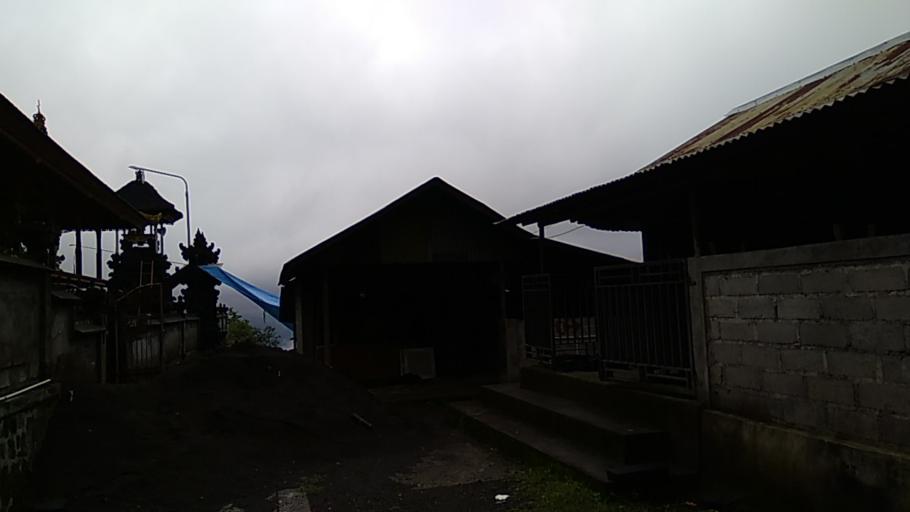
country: ID
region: Bali
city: Tistagede
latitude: -8.3911
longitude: 115.6303
